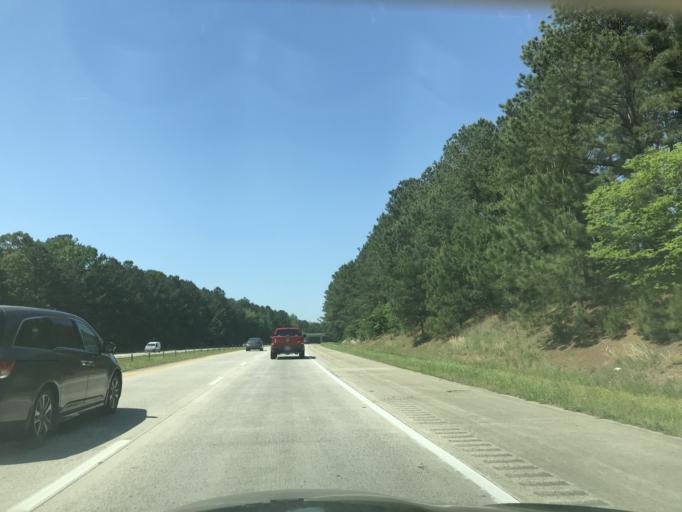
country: US
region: North Carolina
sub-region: Johnston County
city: Benson
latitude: 35.4689
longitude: -78.5478
